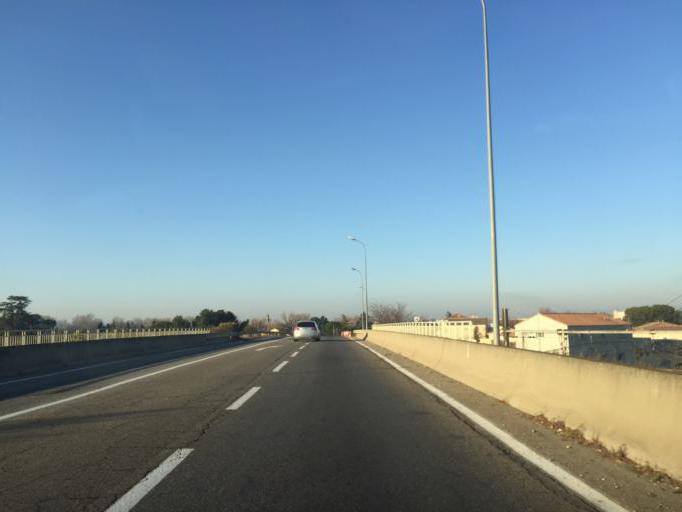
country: FR
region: Provence-Alpes-Cote d'Azur
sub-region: Departement du Vaucluse
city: Le Pontet
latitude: 43.9659
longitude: 4.8573
